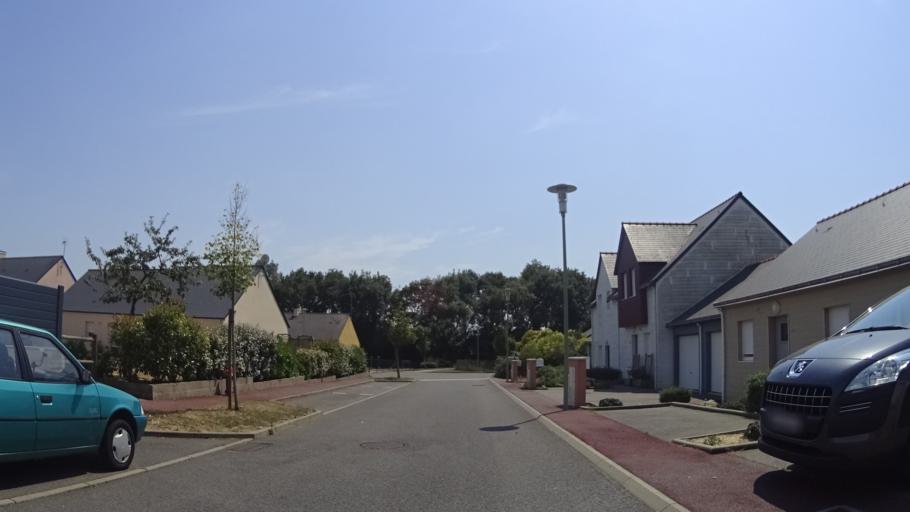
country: FR
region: Pays de la Loire
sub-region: Departement de la Loire-Atlantique
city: Savenay
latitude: 47.3657
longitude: -1.9276
